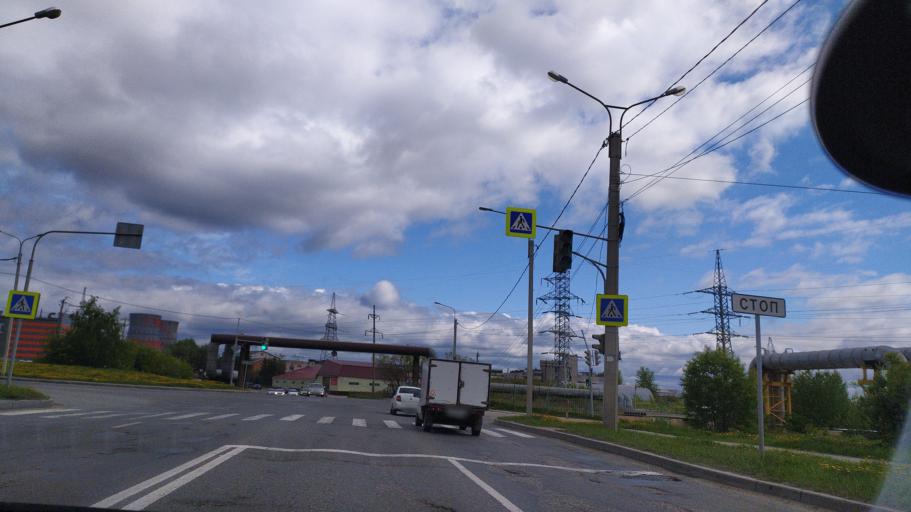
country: RU
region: Chuvashia
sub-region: Cheboksarskiy Rayon
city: Cheboksary
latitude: 56.1164
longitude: 47.3007
